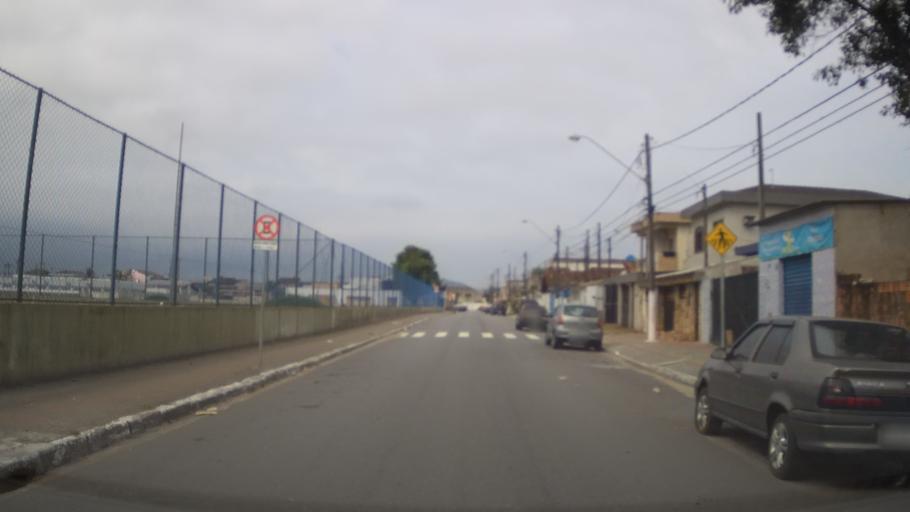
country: BR
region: Sao Paulo
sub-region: Praia Grande
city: Praia Grande
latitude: -24.0090
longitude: -46.4509
